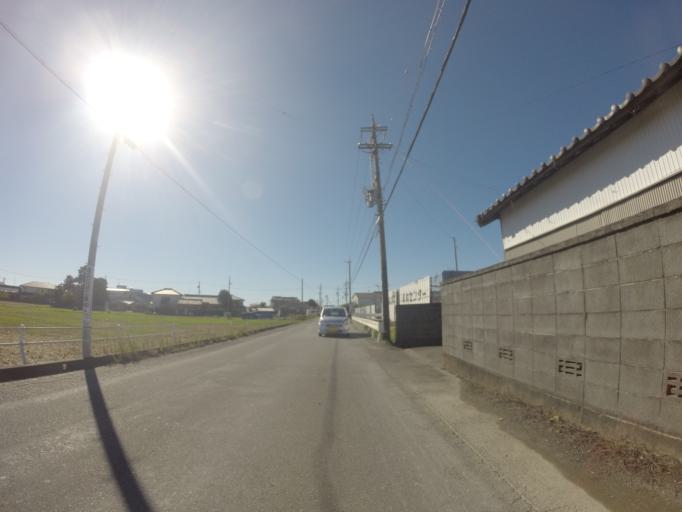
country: JP
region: Shizuoka
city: Fujieda
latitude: 34.8373
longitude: 138.2394
